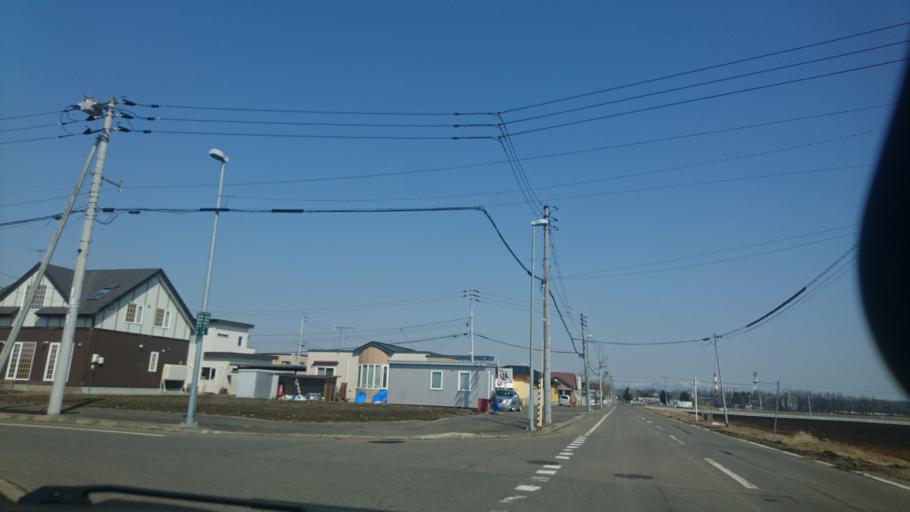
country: JP
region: Hokkaido
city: Obihiro
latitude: 42.9103
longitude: 143.0771
